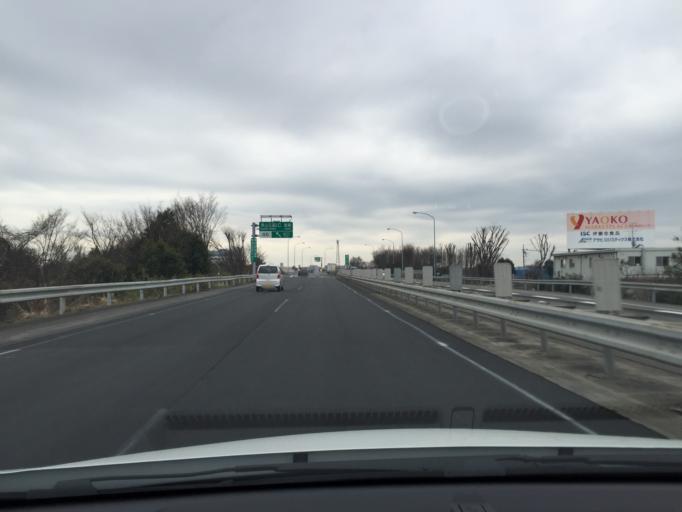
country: JP
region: Saitama
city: Sayama
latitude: 35.8691
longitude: 139.3773
